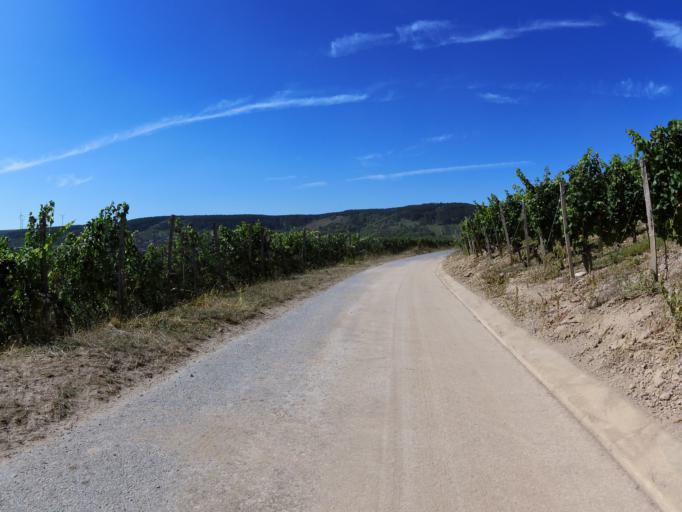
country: DE
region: Bavaria
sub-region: Regierungsbezirk Unterfranken
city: Thungersheim
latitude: 49.8662
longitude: 9.8602
